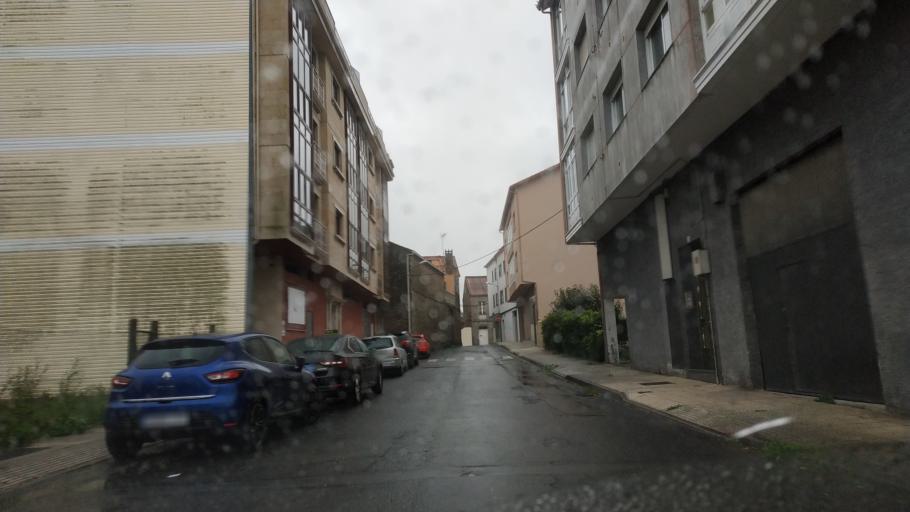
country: ES
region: Galicia
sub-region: Provincia da Coruna
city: Negreira
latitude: 42.9091
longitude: -8.7381
